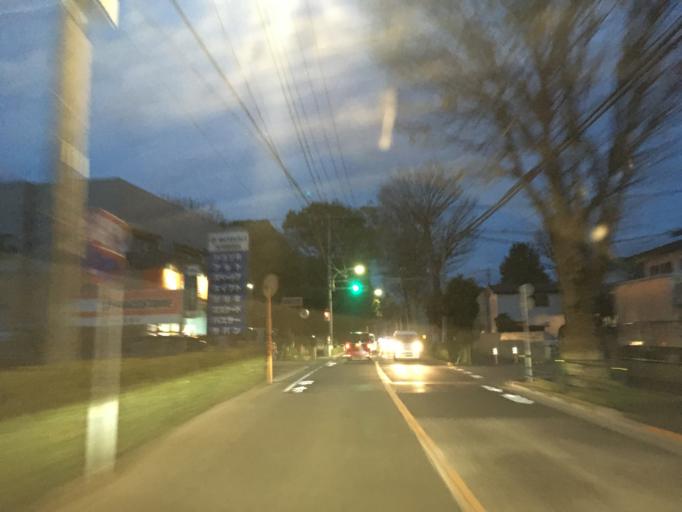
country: JP
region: Tokyo
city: Mitaka-shi
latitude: 35.6833
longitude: 139.5411
